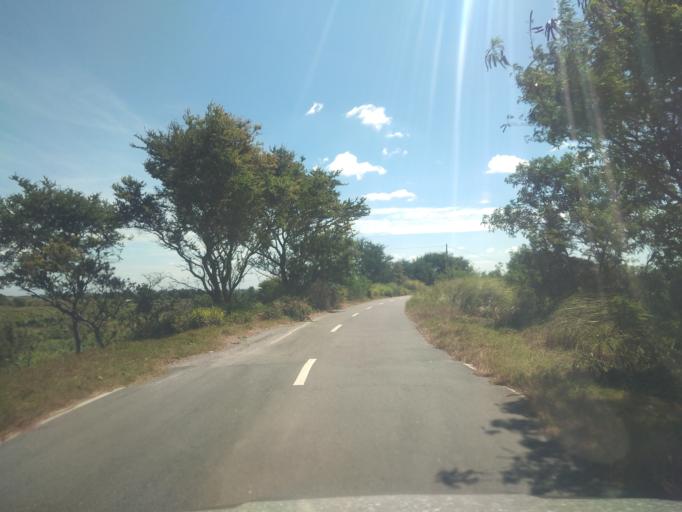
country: PH
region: Central Luzon
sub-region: Province of Pampanga
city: Balas
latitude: 15.0453
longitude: 120.5928
